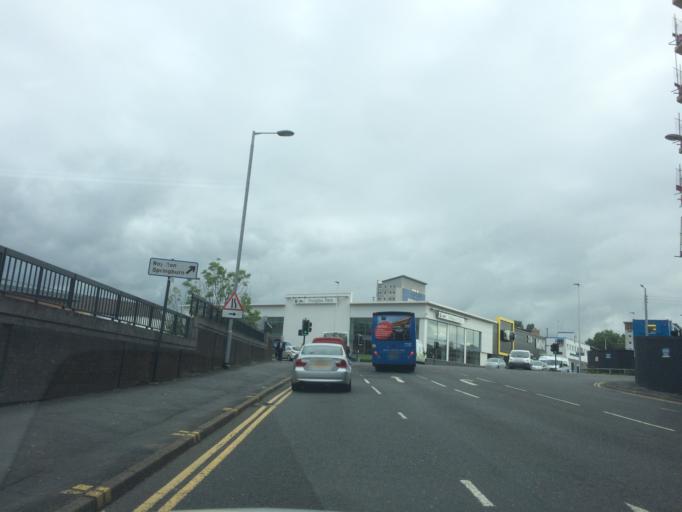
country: GB
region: Scotland
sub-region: Glasgow City
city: Glasgow
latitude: 55.8666
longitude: -4.2481
